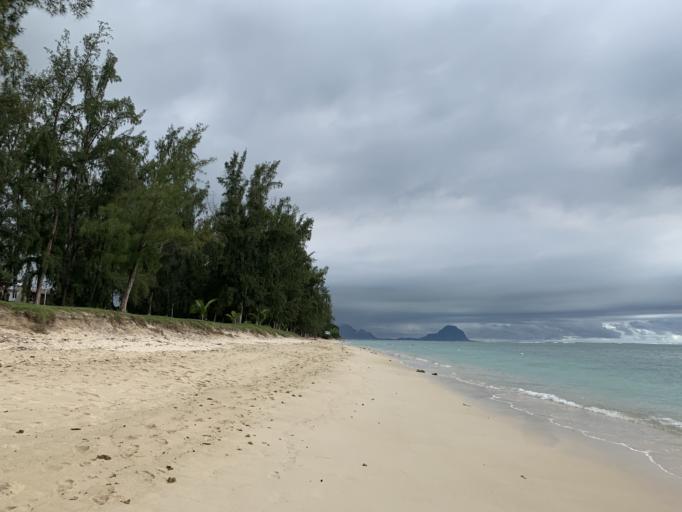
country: MU
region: Black River
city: Flic en Flac
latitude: -20.2887
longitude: 57.3631
